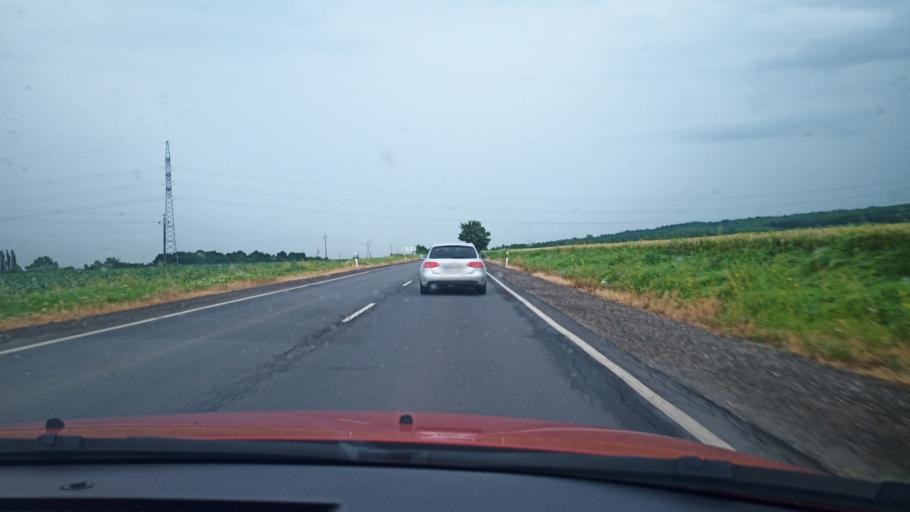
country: HU
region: Borsod-Abauj-Zemplen
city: Malyi
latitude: 48.0431
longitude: 20.8034
